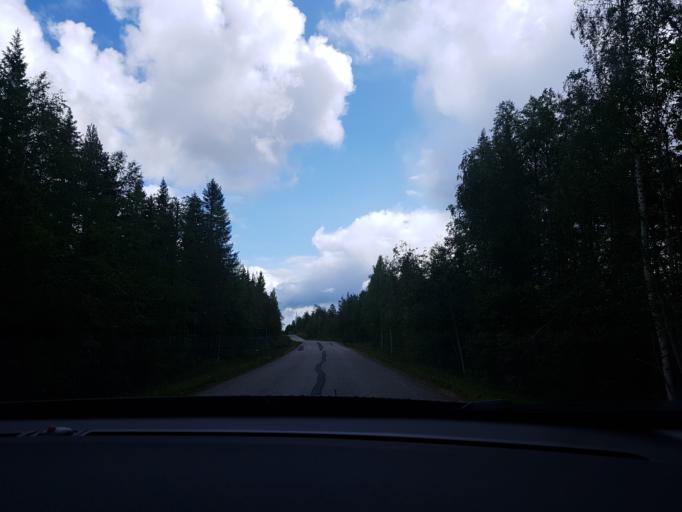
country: FI
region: Kainuu
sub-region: Kehys-Kainuu
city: Kuhmo
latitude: 64.4605
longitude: 29.6040
